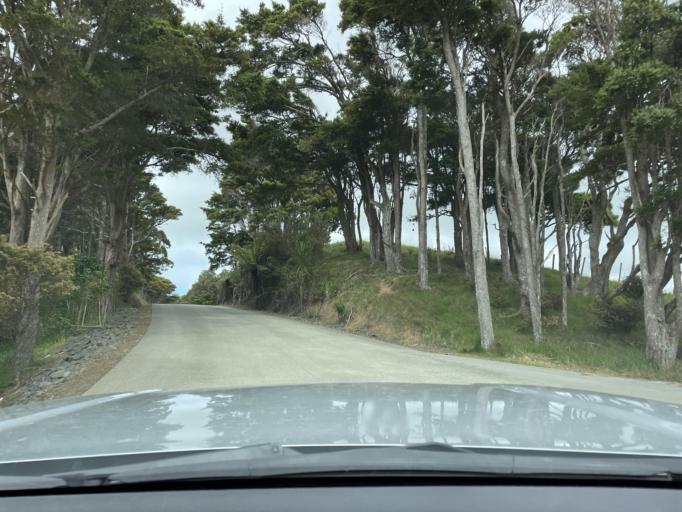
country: NZ
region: Auckland
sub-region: Auckland
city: Wellsford
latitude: -36.1657
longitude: 174.5525
